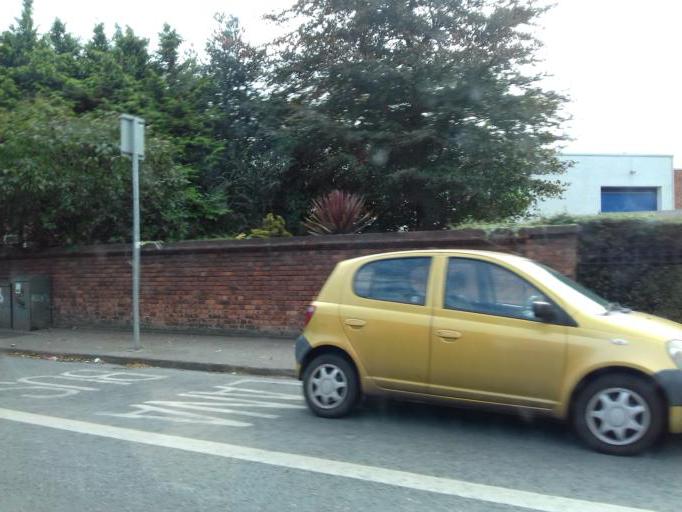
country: IE
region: Leinster
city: Rialto
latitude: 53.3325
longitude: -6.2895
